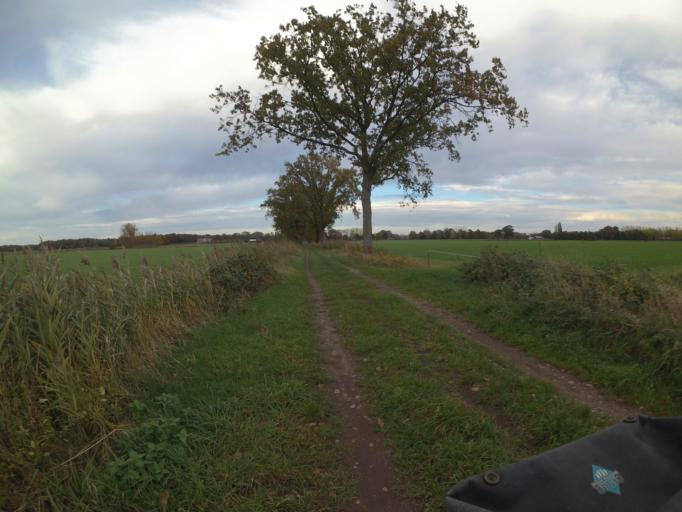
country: NL
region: North Brabant
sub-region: Gemeente Haaren
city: Haaren
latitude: 51.6153
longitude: 5.2636
